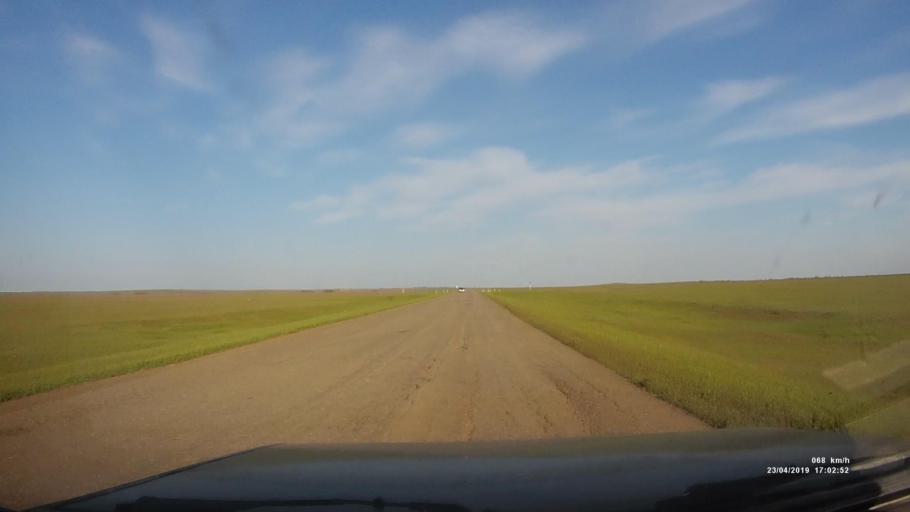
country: RU
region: Kalmykiya
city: Priyutnoye
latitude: 46.2914
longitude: 43.4234
